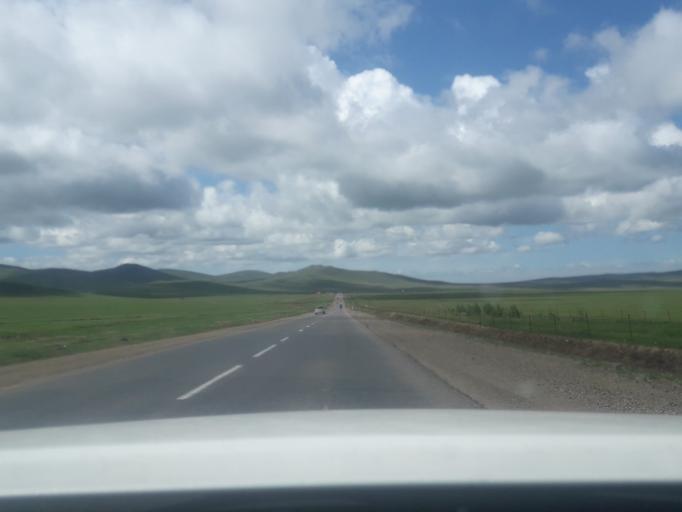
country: MN
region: Central Aimak
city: Altanbulag
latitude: 47.9006
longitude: 106.4660
